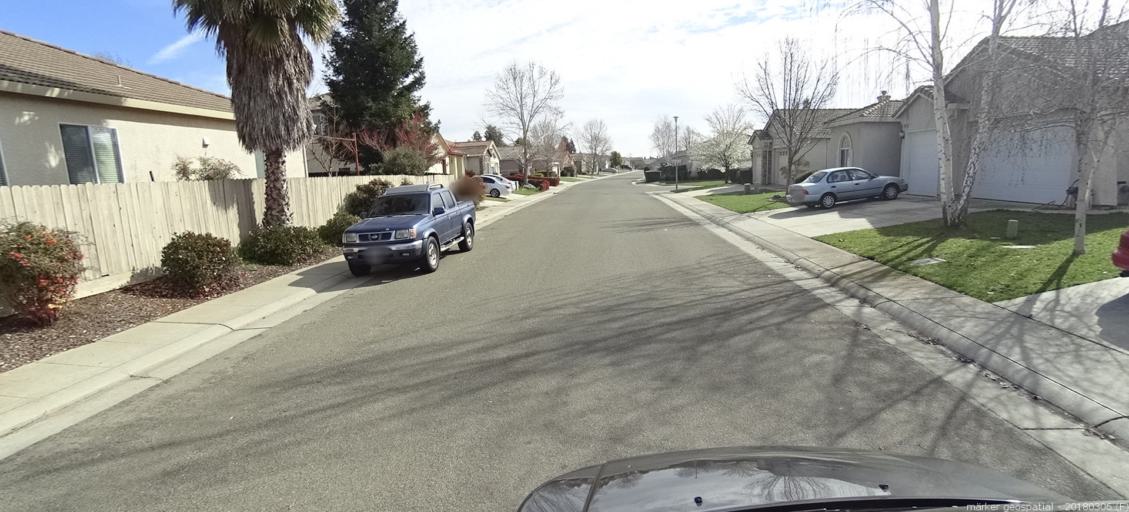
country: US
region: California
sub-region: Sacramento County
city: Vineyard
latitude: 38.4733
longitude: -121.3152
